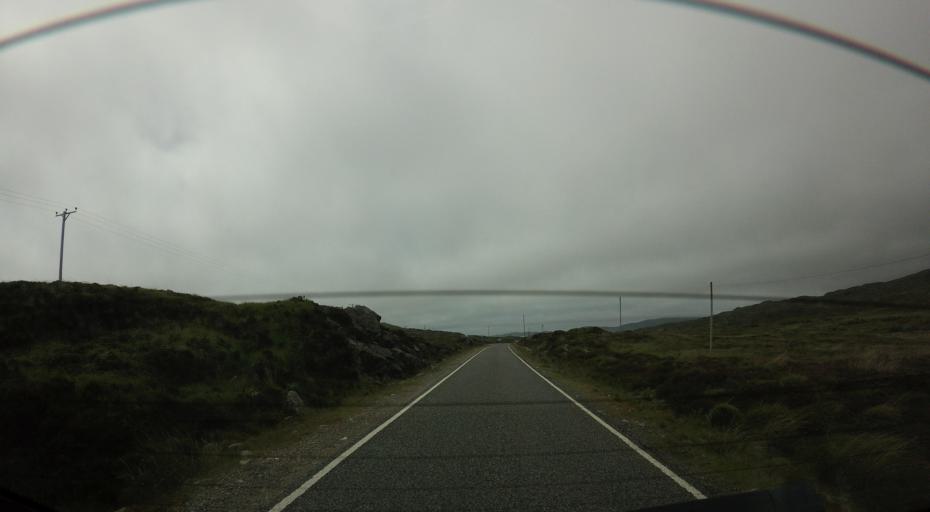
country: GB
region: Scotland
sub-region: Eilean Siar
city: Harris
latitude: 57.8676
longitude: -6.8941
